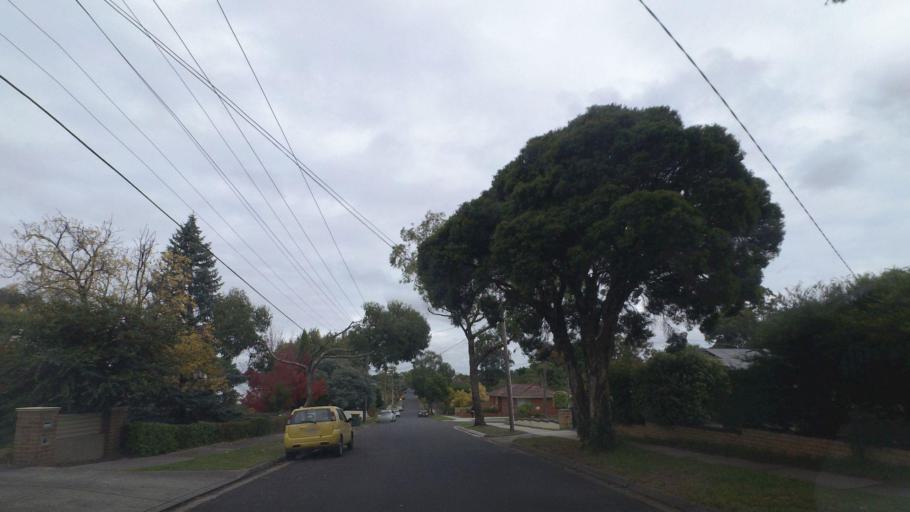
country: AU
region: Victoria
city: Forest Hill
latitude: -37.8317
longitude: 145.1838
